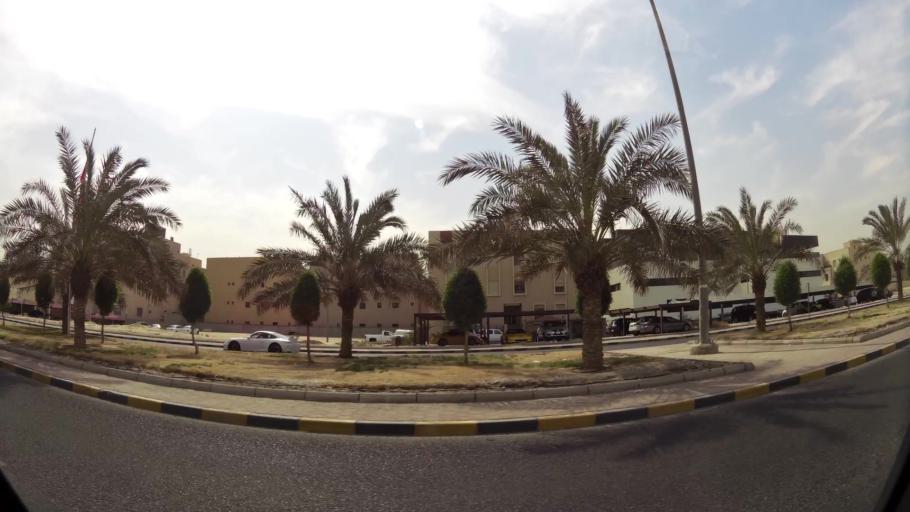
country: KW
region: Al Farwaniyah
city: Janub as Surrah
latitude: 29.2851
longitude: 48.0035
